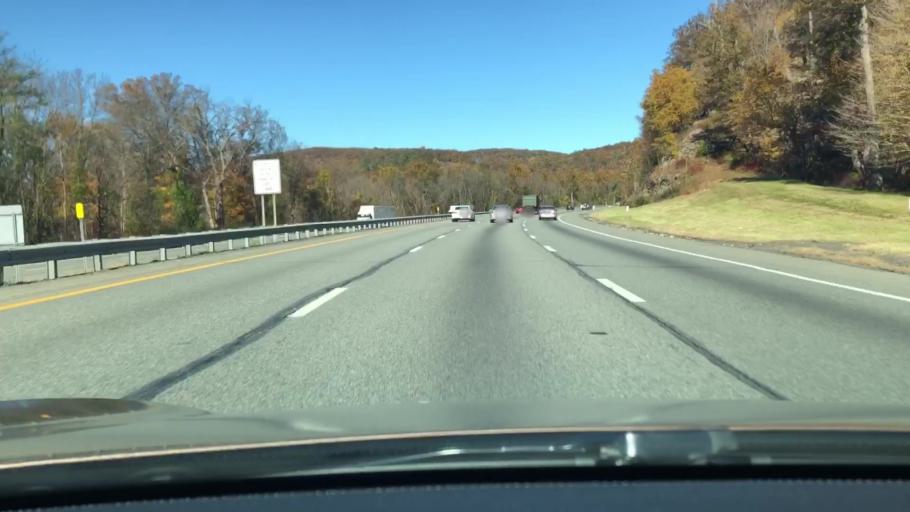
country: US
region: New York
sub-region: Rockland County
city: Sloatsburg
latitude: 41.2213
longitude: -74.1842
